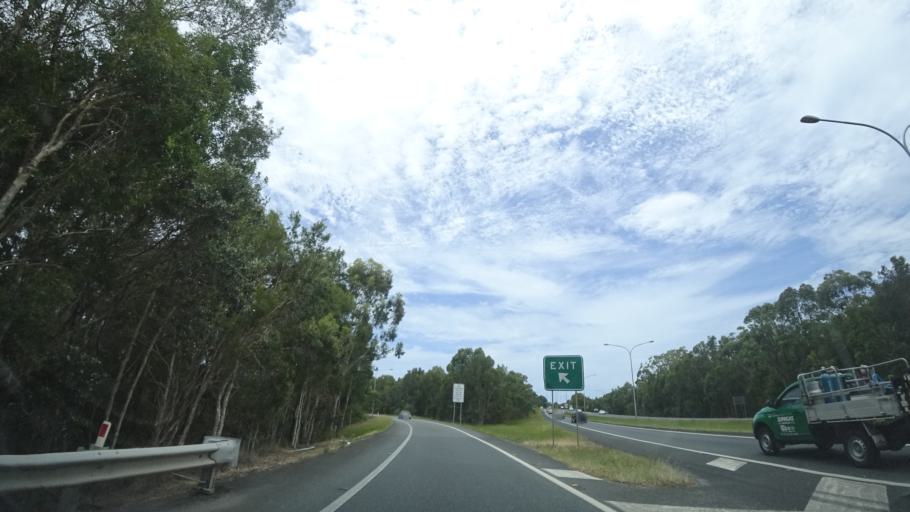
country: AU
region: Queensland
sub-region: Sunshine Coast
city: Mooloolaba
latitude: -26.6954
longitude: 153.1085
